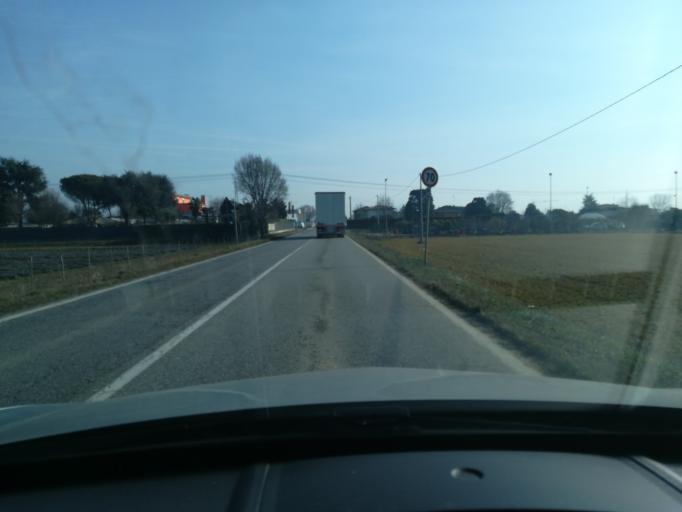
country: IT
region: Lombardy
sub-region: Provincia di Bergamo
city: Palosco
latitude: 45.5995
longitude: 9.8606
